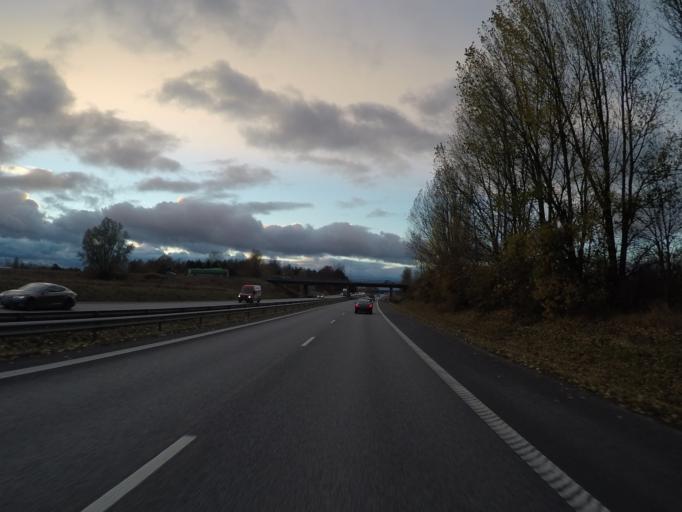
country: SE
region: Skane
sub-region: Kristianstads Kommun
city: Kristianstad
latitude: 56.0170
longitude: 14.1272
